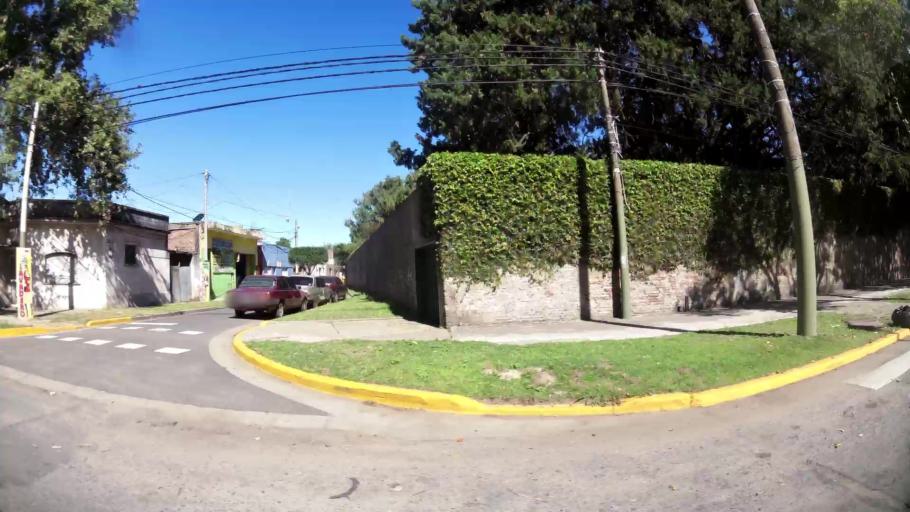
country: AR
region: Santa Fe
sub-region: Departamento de Rosario
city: Rosario
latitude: -32.9523
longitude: -60.6825
